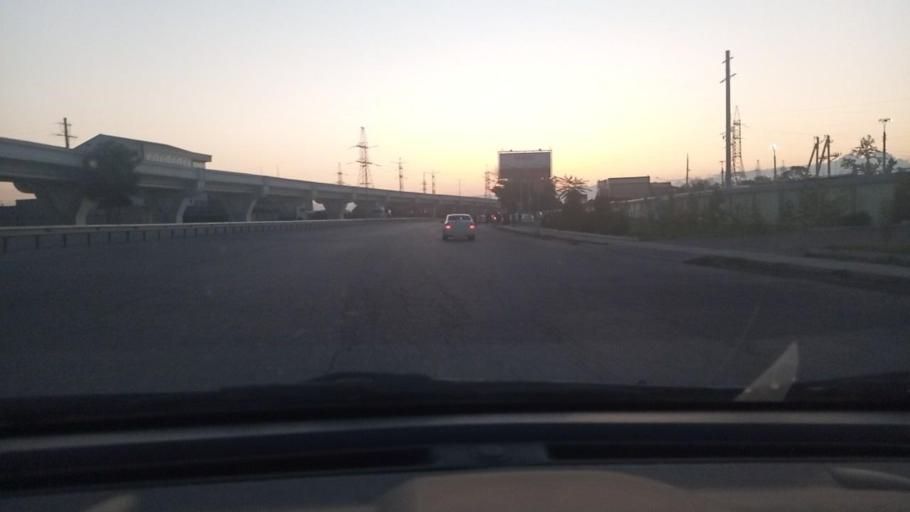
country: UZ
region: Toshkent Shahri
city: Bektemir
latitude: 41.2432
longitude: 69.3378
